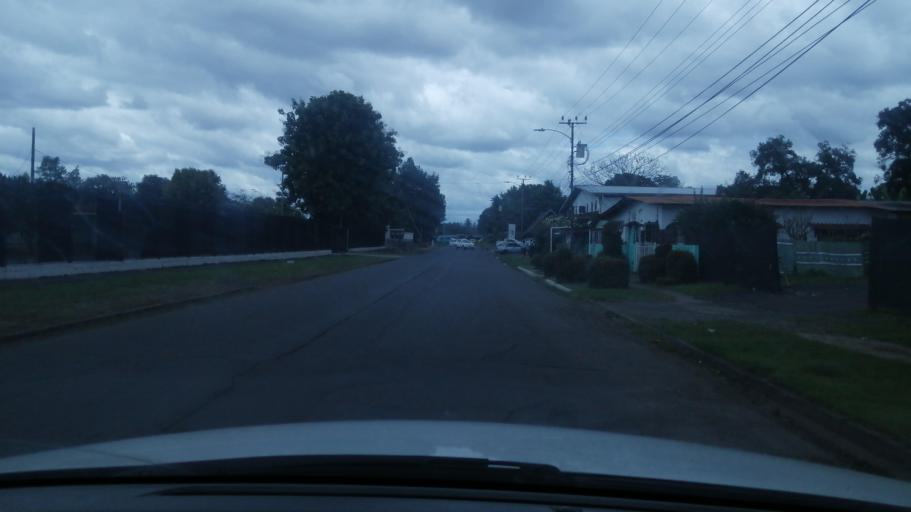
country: PA
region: Chiriqui
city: David
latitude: 8.4216
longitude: -82.4363
